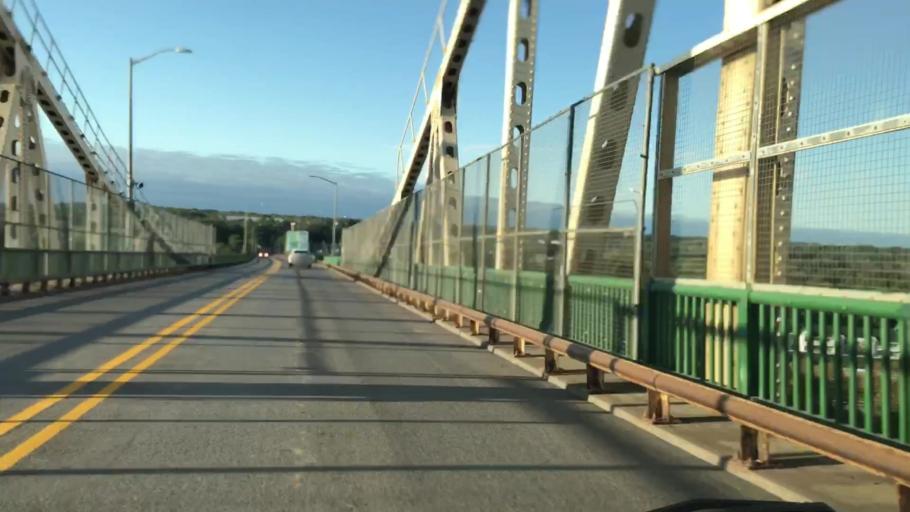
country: US
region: Michigan
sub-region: Chippewa County
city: Sault Ste. Marie
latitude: 46.5019
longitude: -84.3636
